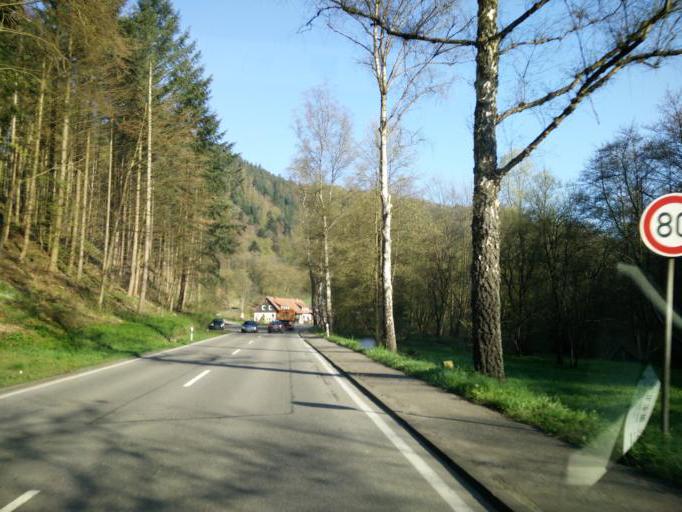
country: DE
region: Baden-Wuerttemberg
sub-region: Karlsruhe Region
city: Bad Liebenzell
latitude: 48.7595
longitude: 8.7313
